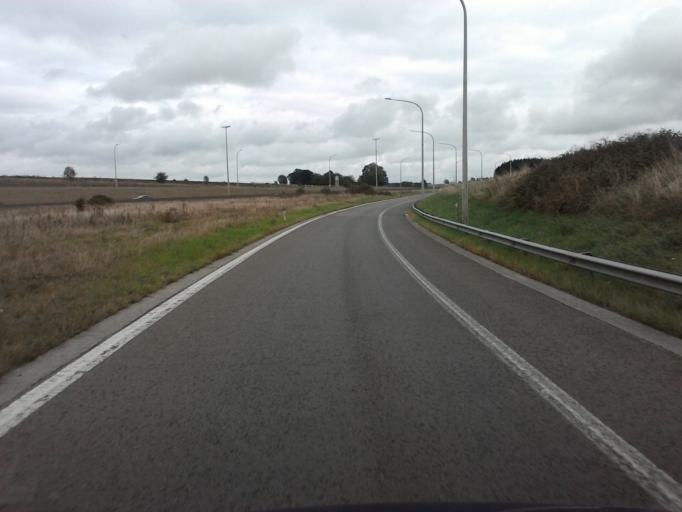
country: BE
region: Wallonia
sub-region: Province du Luxembourg
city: Bertrix
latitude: 49.9002
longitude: 5.3266
